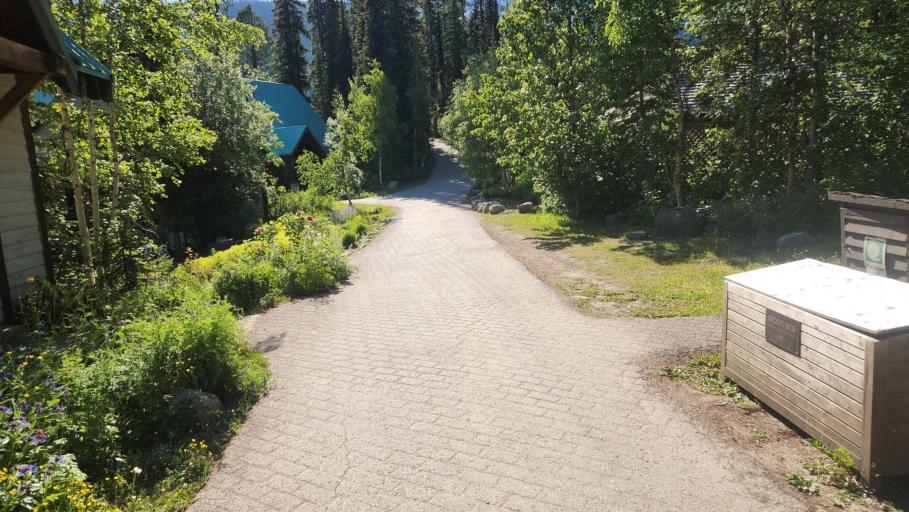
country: CA
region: Alberta
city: Lake Louise
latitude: 51.4396
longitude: -116.5372
